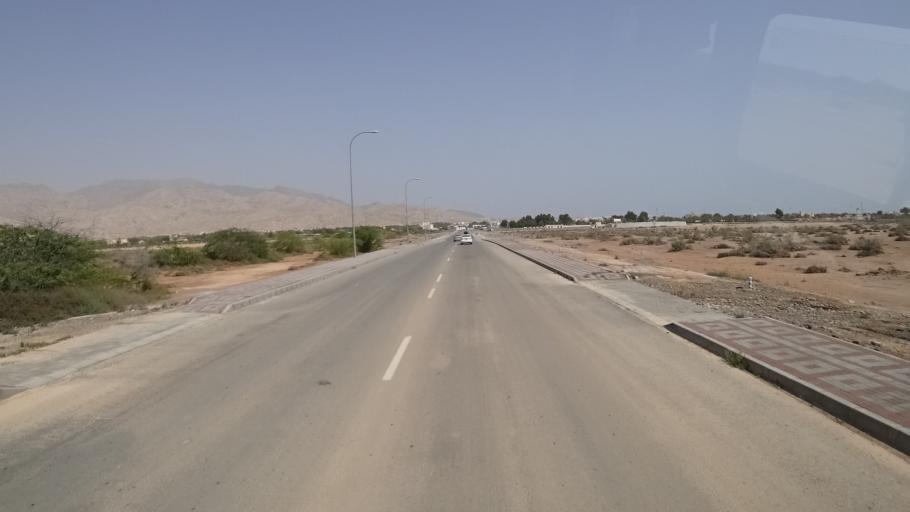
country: OM
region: Muhafazat Masqat
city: Muscat
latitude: 23.2486
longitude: 58.9113
